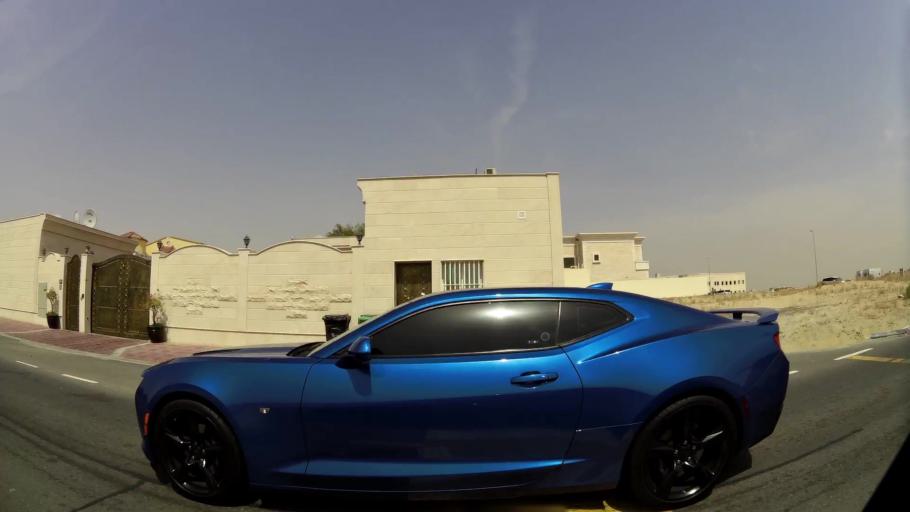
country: AE
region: Ash Shariqah
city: Sharjah
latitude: 25.2395
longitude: 55.4418
